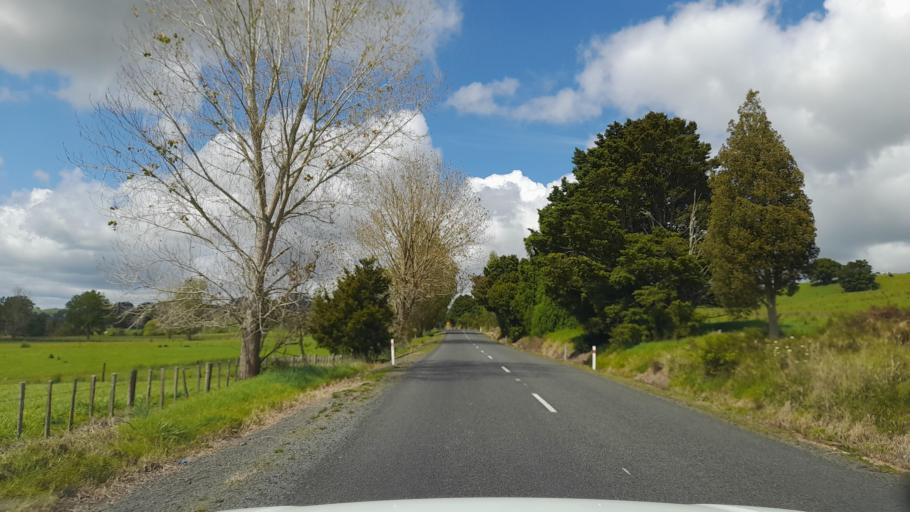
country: NZ
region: Northland
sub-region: Whangarei
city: Maungatapere
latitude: -35.6269
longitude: 174.0961
